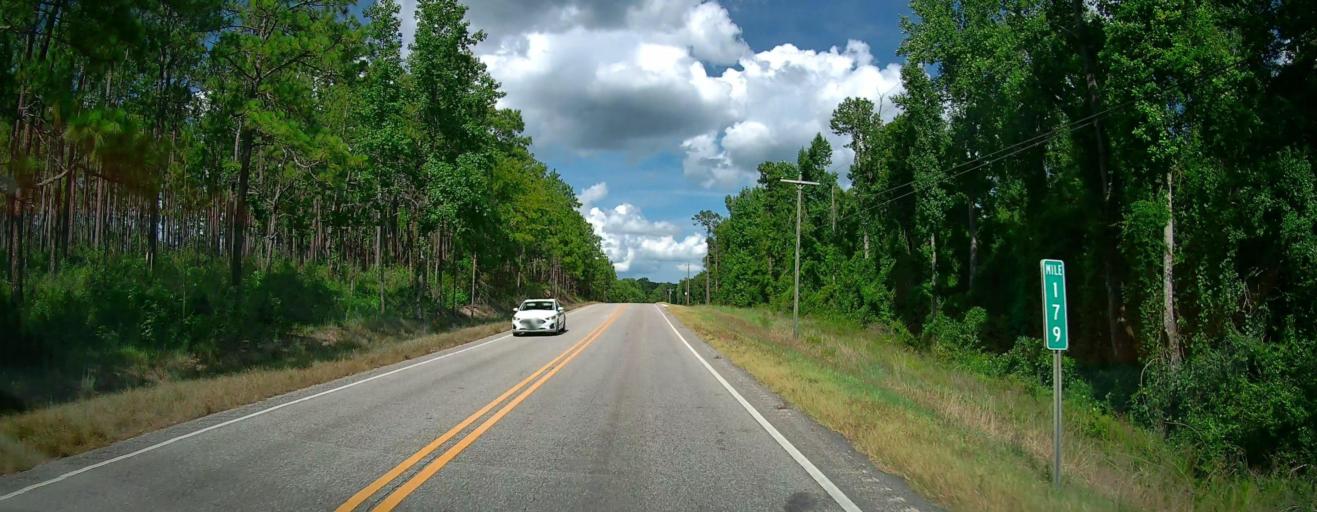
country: US
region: Alabama
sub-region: Macon County
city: Tuskegee
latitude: 32.4600
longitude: -85.6158
